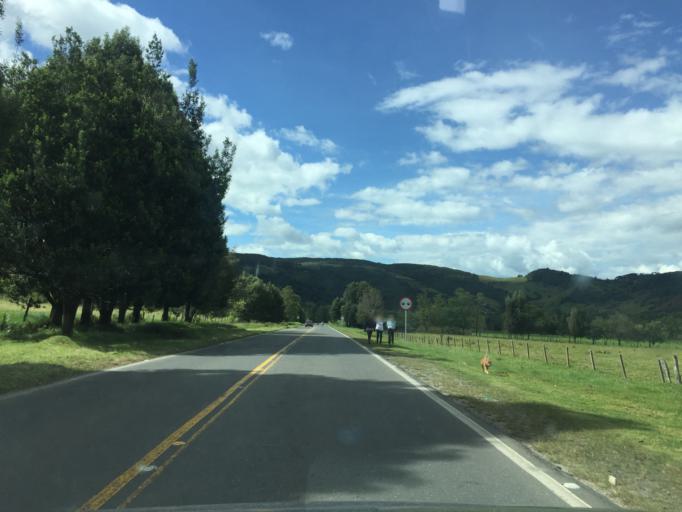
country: CO
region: Boyaca
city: Arcabuco
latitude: 5.7862
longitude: -73.4630
